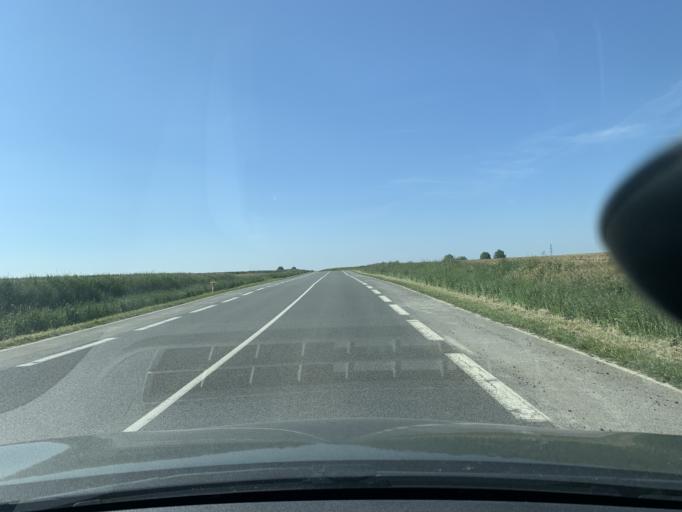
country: FR
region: Nord-Pas-de-Calais
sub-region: Departement du Nord
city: Rumilly-en-Cambresis
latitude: 50.1237
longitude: 3.2461
